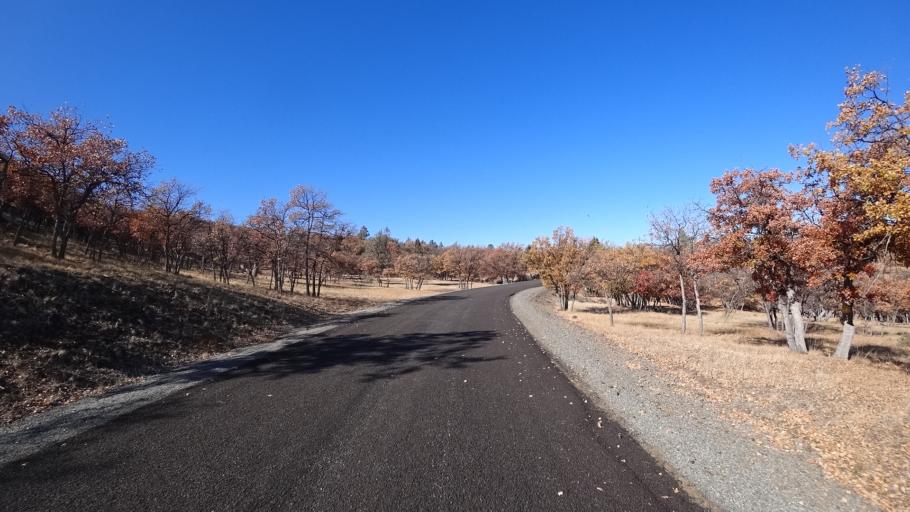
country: US
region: California
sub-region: Siskiyou County
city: Montague
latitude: 41.8782
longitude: -122.4896
